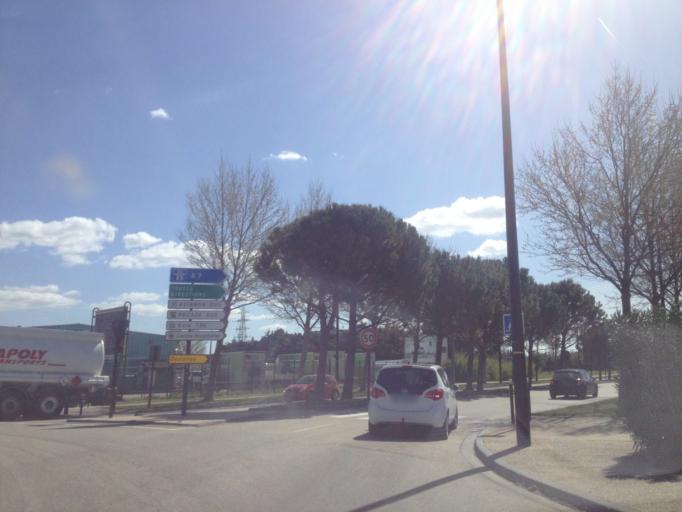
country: FR
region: Provence-Alpes-Cote d'Azur
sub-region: Departement du Vaucluse
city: Avignon
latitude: 43.9302
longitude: 4.7840
